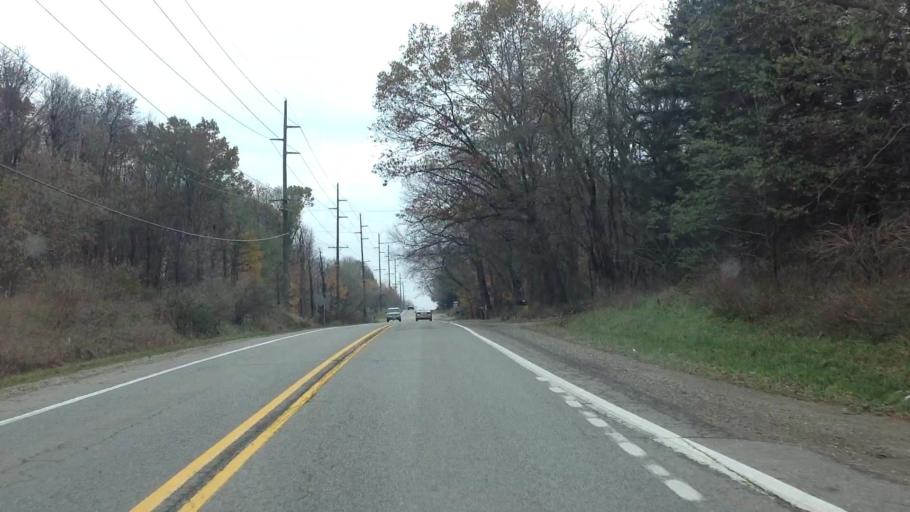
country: US
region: Michigan
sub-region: Oakland County
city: Milford
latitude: 42.6162
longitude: -83.6607
